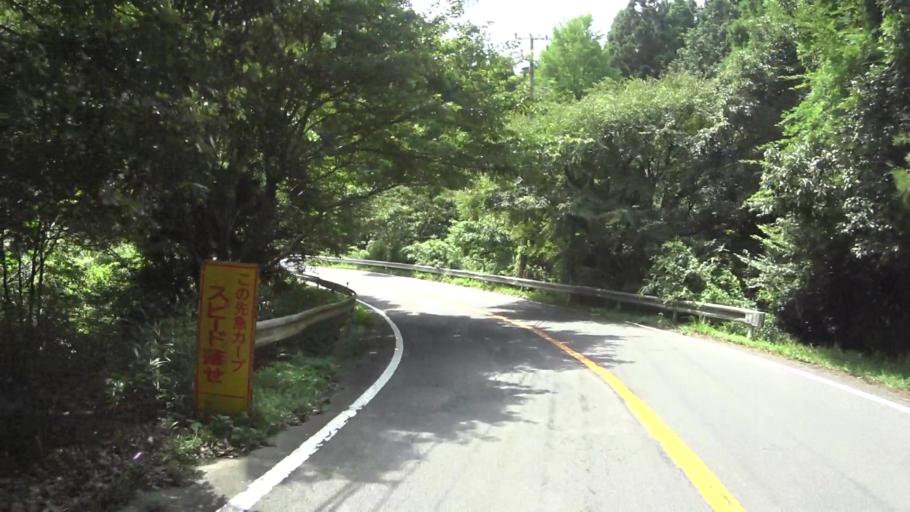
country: JP
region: Kyoto
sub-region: Kyoto-shi
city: Kamigyo-ku
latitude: 35.1083
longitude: 135.8140
